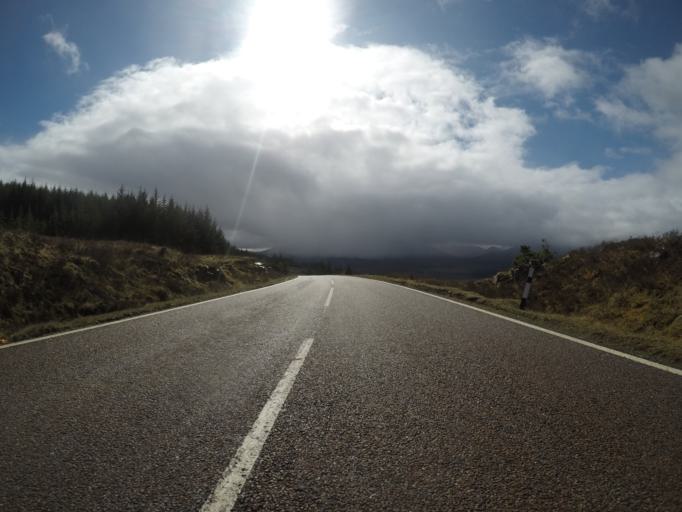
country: GB
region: Scotland
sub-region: Highland
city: Spean Bridge
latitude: 57.0923
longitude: -4.9860
